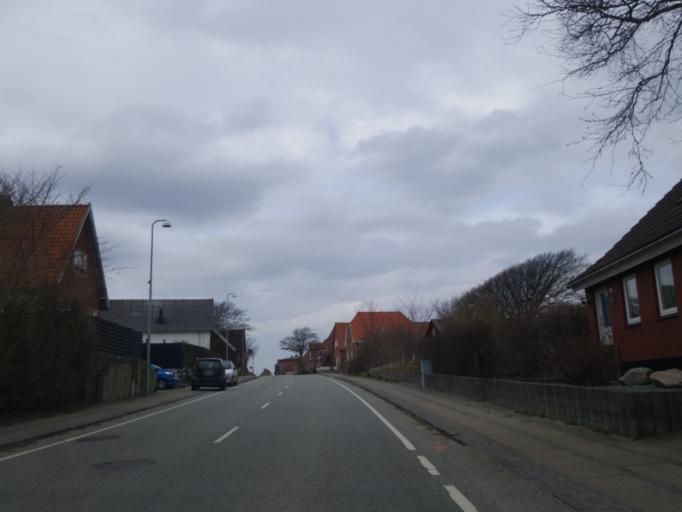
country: DK
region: Central Jutland
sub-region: Lemvig Kommune
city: Lemvig
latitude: 56.4333
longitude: 8.2076
